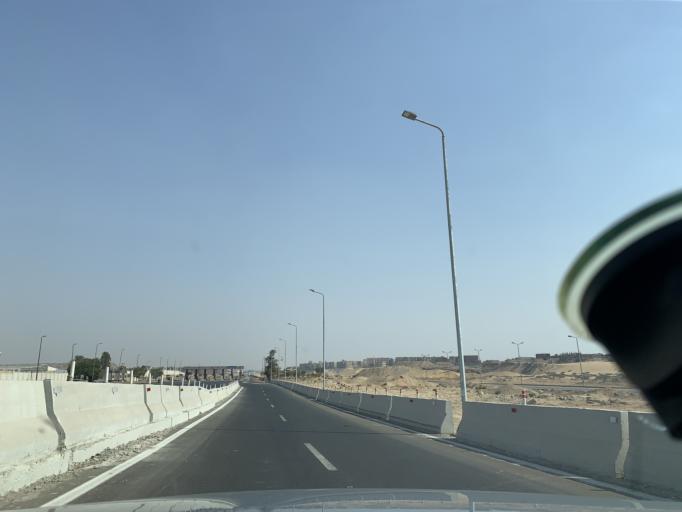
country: EG
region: Muhafazat al Qalyubiyah
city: Al Khankah
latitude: 30.1999
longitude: 31.4203
